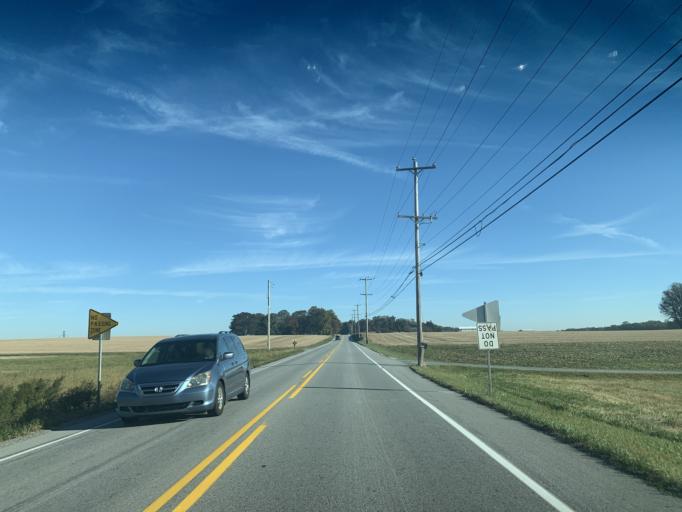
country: US
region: Pennsylvania
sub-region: Chester County
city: Parkesburg
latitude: 39.8996
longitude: -75.9132
